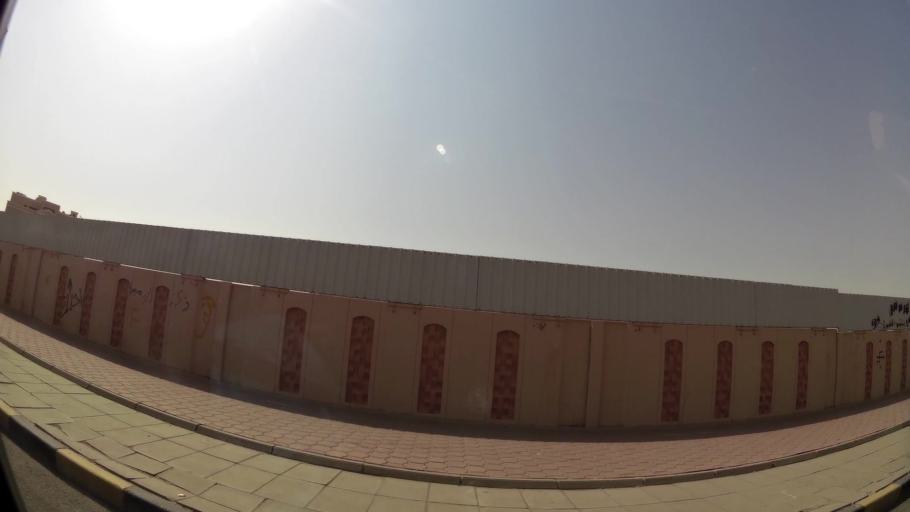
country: KW
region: Muhafazat al Jahra'
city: Al Jahra'
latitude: 29.3201
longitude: 47.6772
